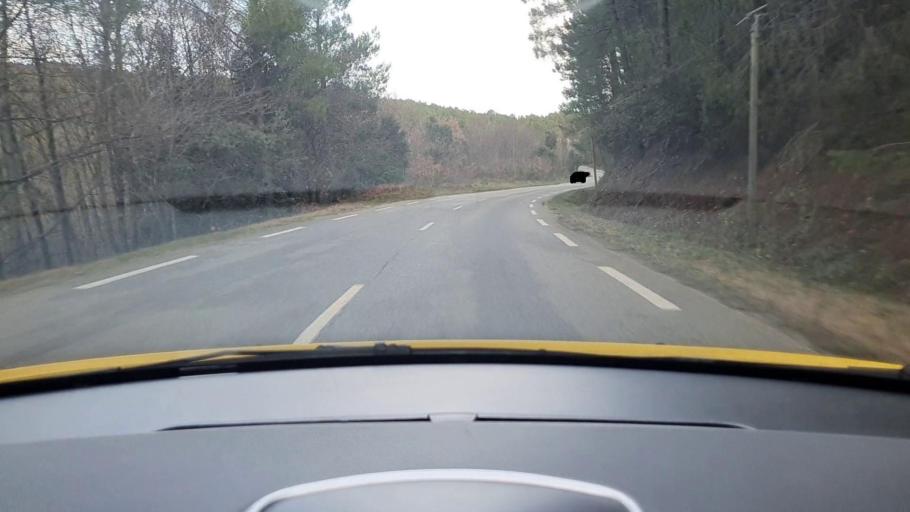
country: FR
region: Languedoc-Roussillon
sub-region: Departement du Gard
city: Les Salles-du-Gardon
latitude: 44.2563
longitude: 4.0458
